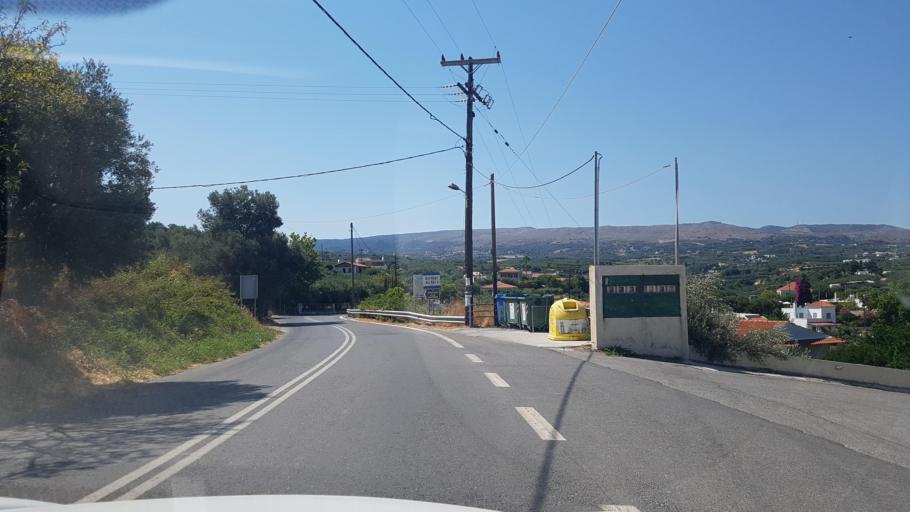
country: GR
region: Crete
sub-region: Nomos Rethymnis
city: Panormos
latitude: 35.3714
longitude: 24.5966
